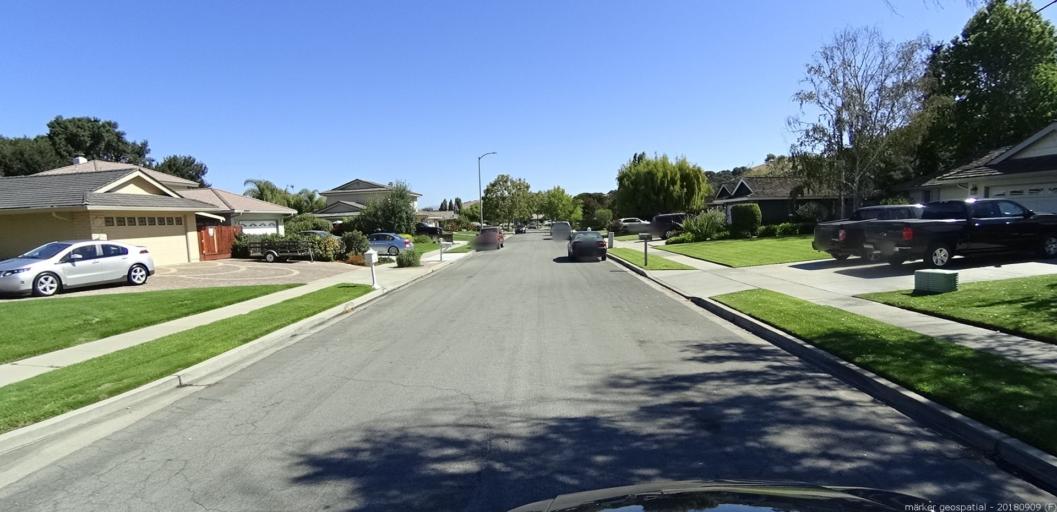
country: US
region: California
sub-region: Monterey County
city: Carmel Valley Village
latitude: 36.5904
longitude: -121.7101
